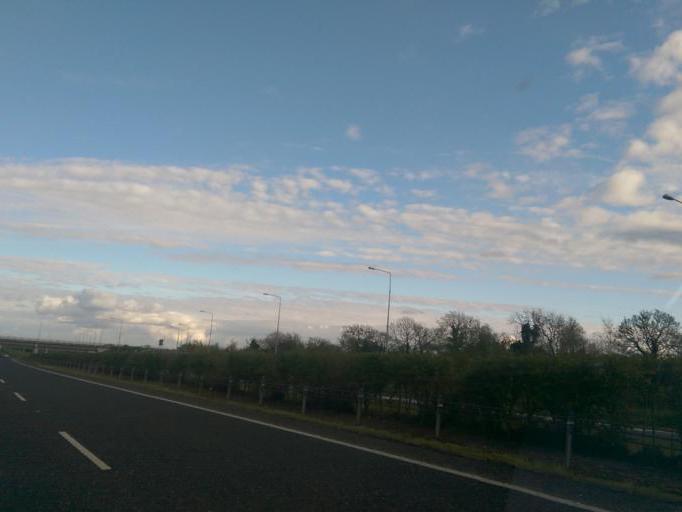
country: IE
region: Leinster
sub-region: Kildare
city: Kilcock
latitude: 53.4042
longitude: -6.6942
